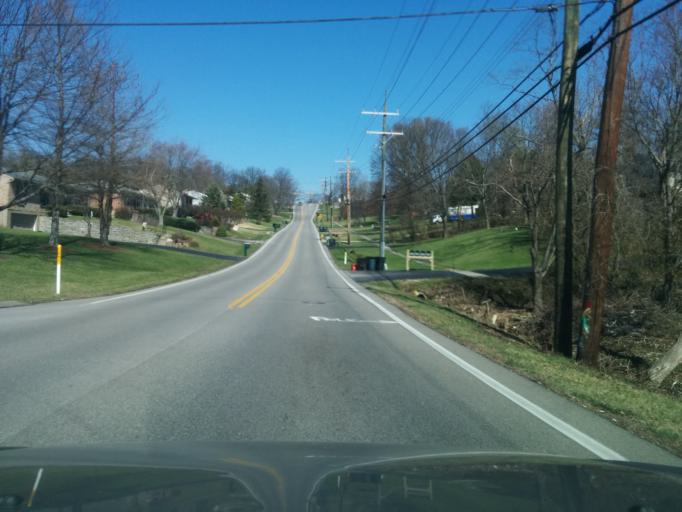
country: US
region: Ohio
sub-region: Hamilton County
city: Dent
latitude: 39.1915
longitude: -84.6275
